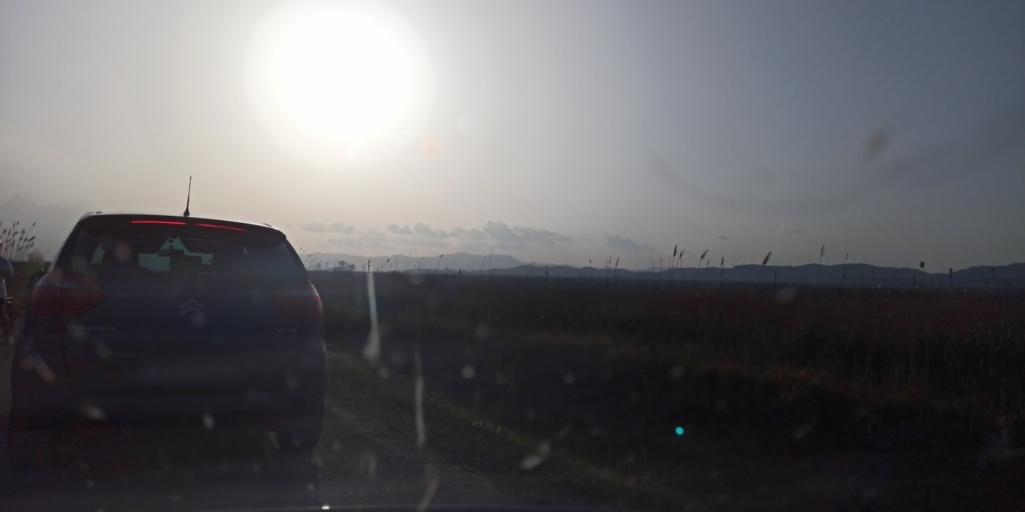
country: ES
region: Catalonia
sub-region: Provincia de Tarragona
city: L'Ampolla
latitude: 40.7855
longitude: 0.7021
